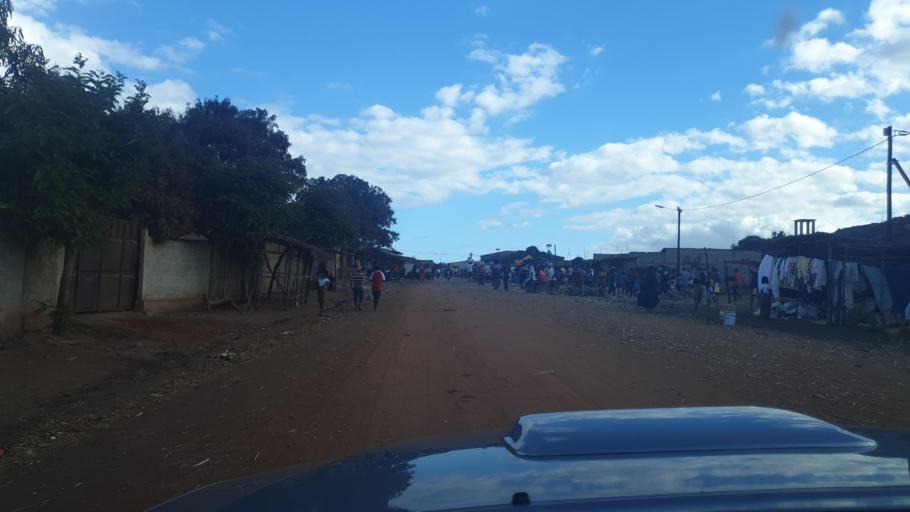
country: MZ
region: Nampula
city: Nampula
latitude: -15.1016
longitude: 39.2215
